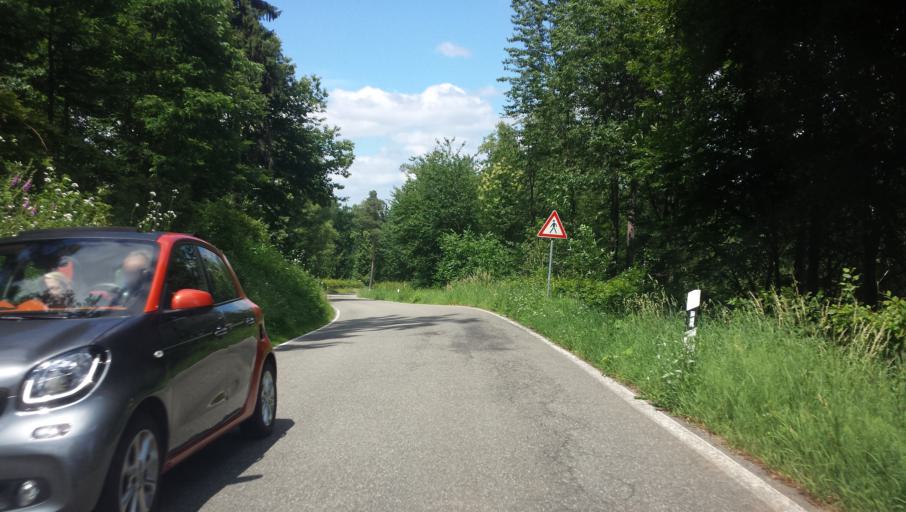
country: DE
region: Rheinland-Pfalz
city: Wernersberg
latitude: 49.1899
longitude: 7.9506
